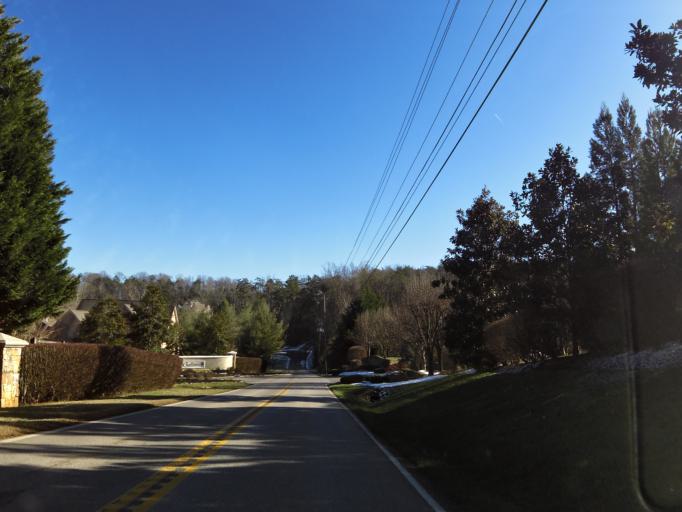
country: US
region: Tennessee
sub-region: Knox County
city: Knoxville
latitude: 35.9060
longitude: -83.9987
